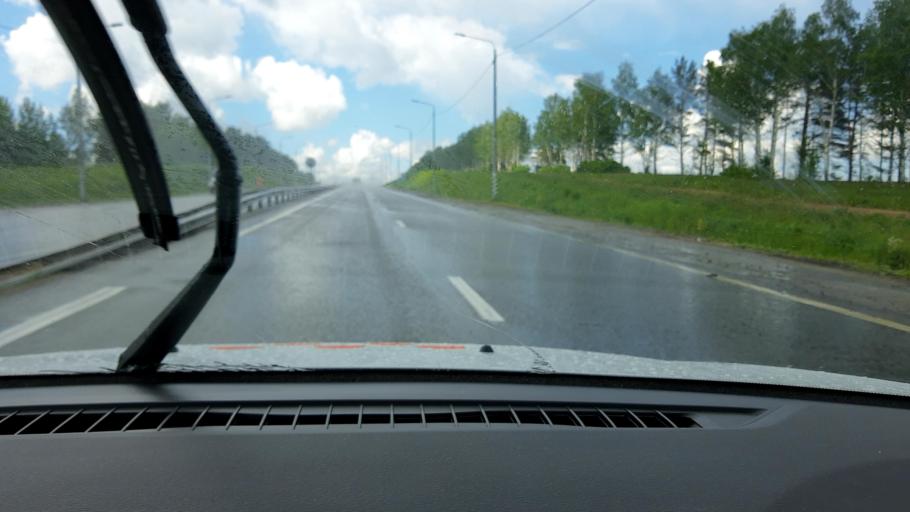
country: RU
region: Nizjnij Novgorod
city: Dal'neye Konstantinovo
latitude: 55.9908
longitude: 43.9696
